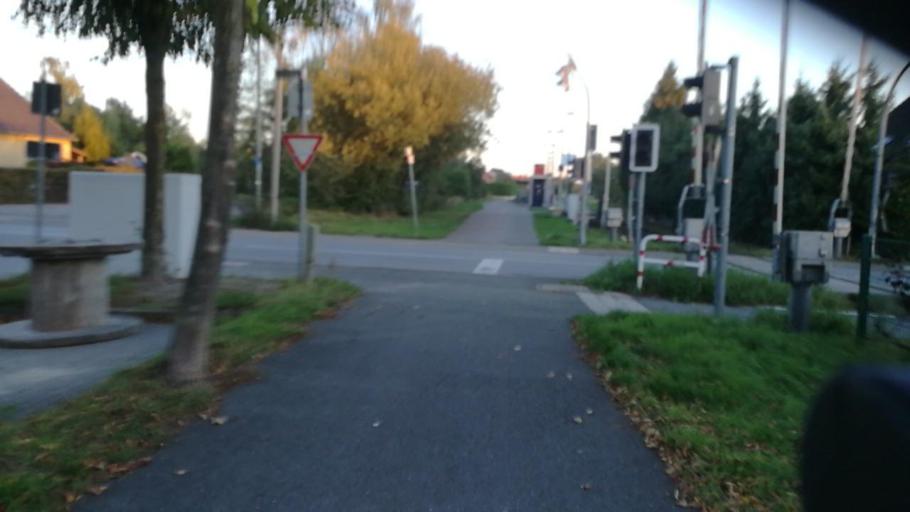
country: DE
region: North Rhine-Westphalia
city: Halle
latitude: 52.0371
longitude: 8.3836
